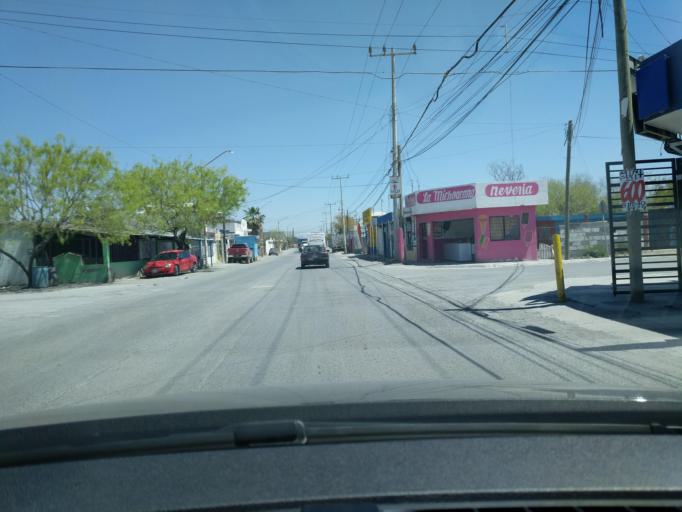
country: MX
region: Nuevo Leon
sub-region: Salinas Victoria
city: Emiliano Zapata
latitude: 25.9088
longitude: -100.2782
